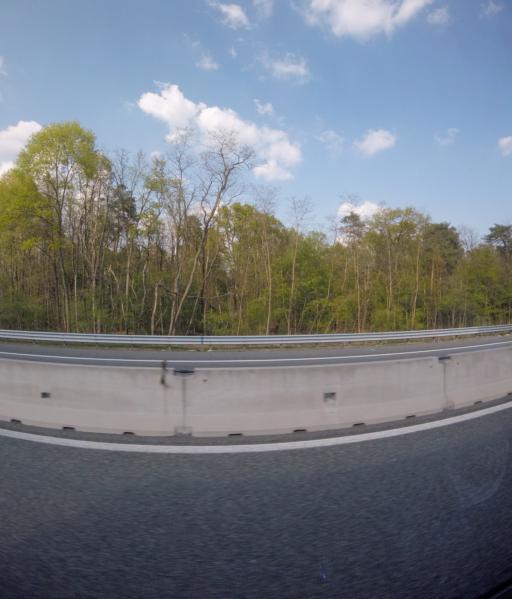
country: IT
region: Lombardy
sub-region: Provincia di Varese
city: Arsago Seprio
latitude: 45.6984
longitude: 8.7458
